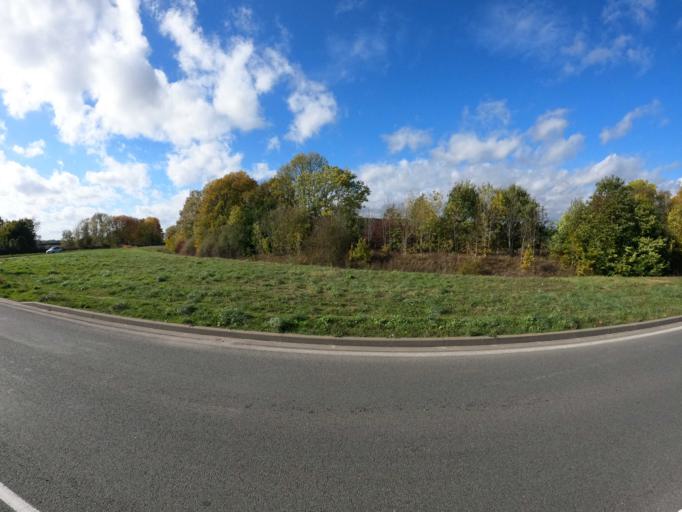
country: FR
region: Ile-de-France
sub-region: Departement de Seine-et-Marne
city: Coupvray
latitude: 48.8836
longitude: 2.8065
